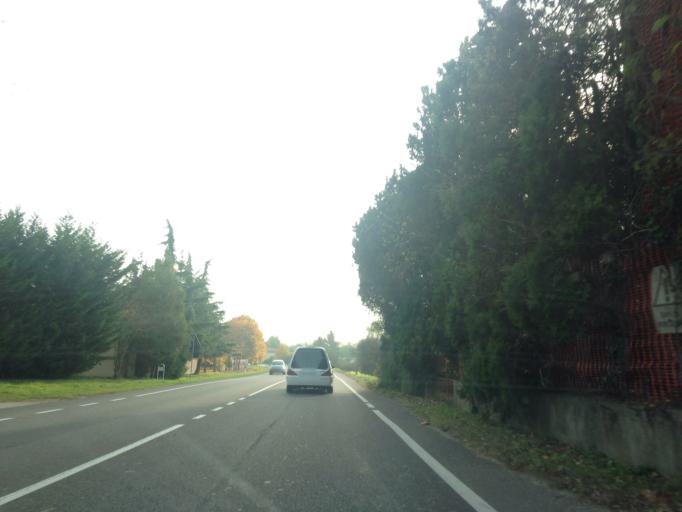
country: IT
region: Veneto
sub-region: Provincia di Treviso
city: Portobuffole
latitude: 45.8559
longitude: 12.5360
